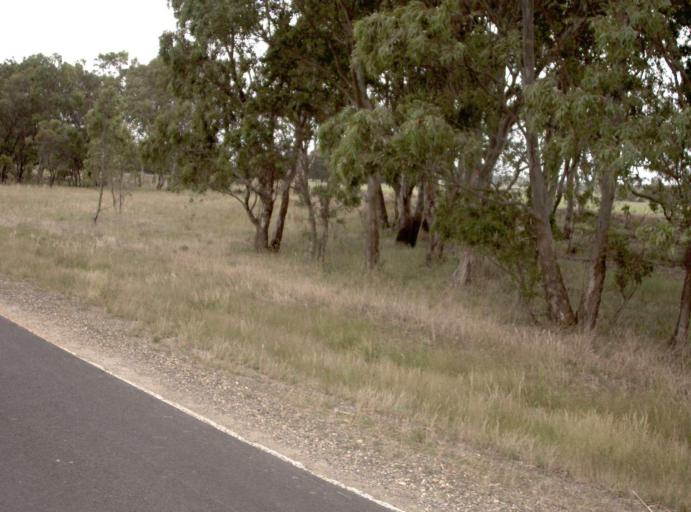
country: AU
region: Victoria
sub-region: Wellington
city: Heyfield
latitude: -38.0410
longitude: 146.7671
